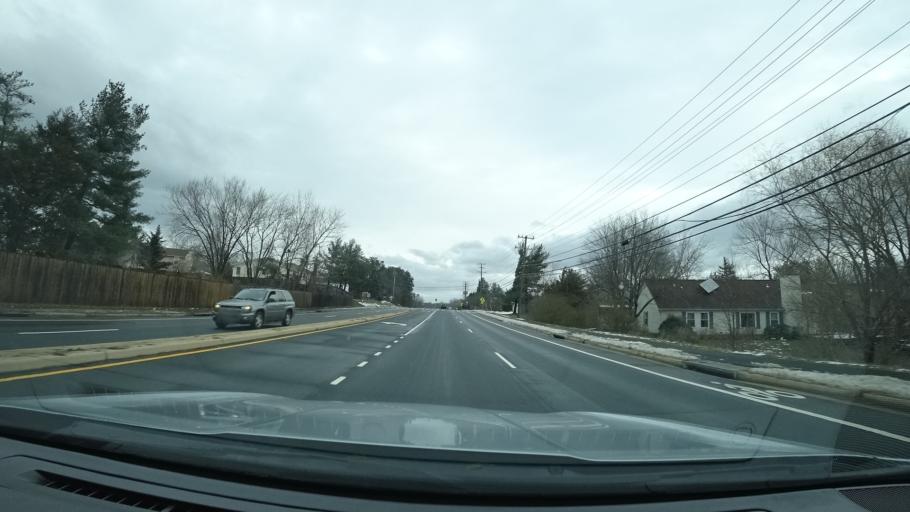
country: US
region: Virginia
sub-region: Fairfax County
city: Dranesville
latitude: 39.0015
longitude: -77.3759
